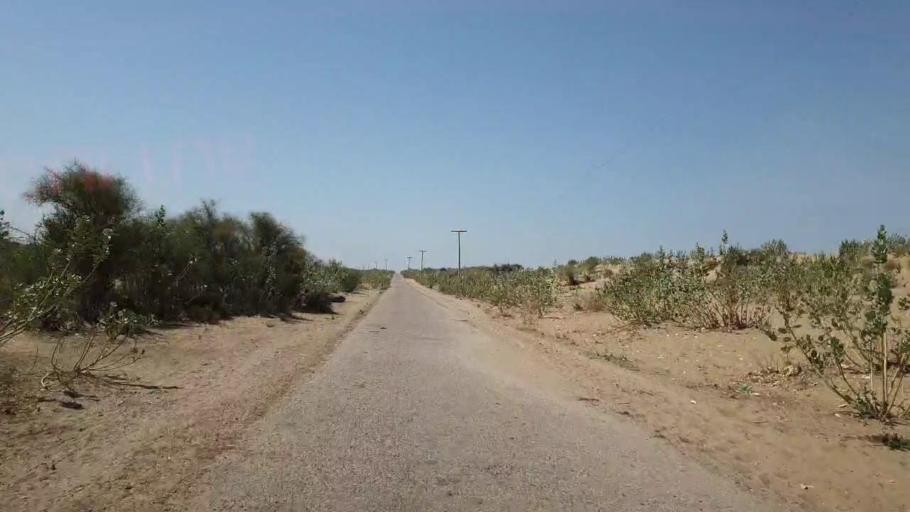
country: PK
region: Sindh
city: Umarkot
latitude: 25.1649
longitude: 69.9627
